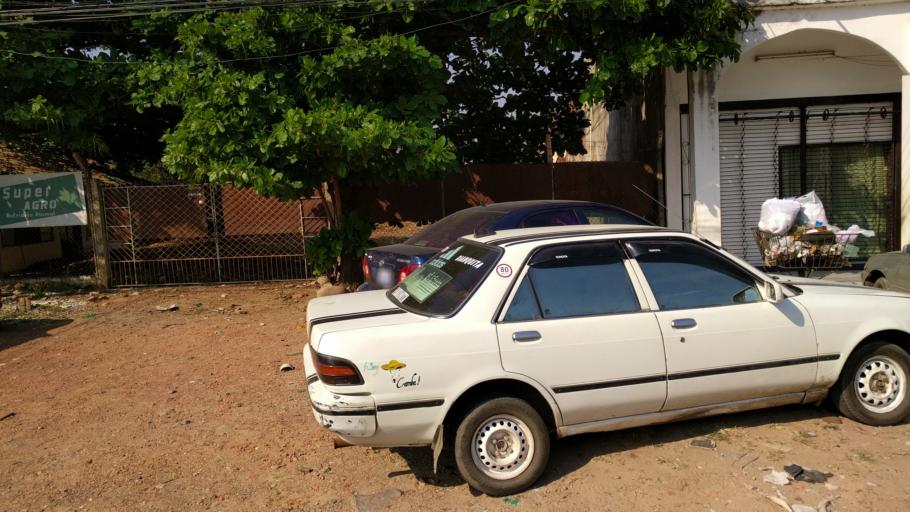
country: BO
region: Santa Cruz
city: Santa Cruz de la Sierra
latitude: -17.7755
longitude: -63.1536
